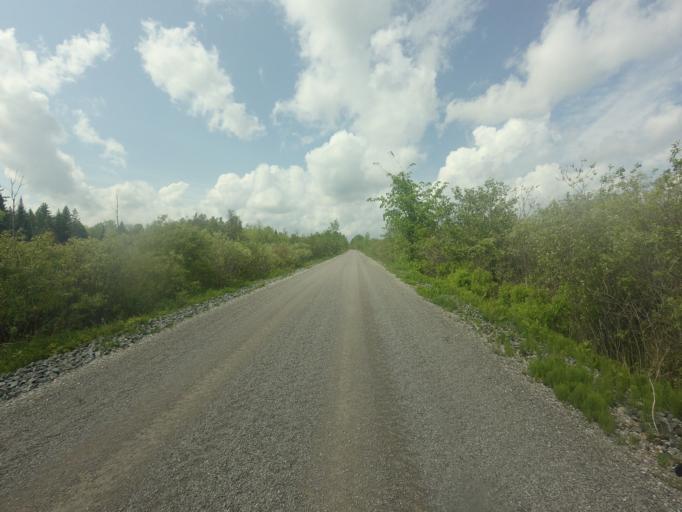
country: CA
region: Ontario
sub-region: Lanark County
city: Smiths Falls
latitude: 45.0129
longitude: -76.0717
